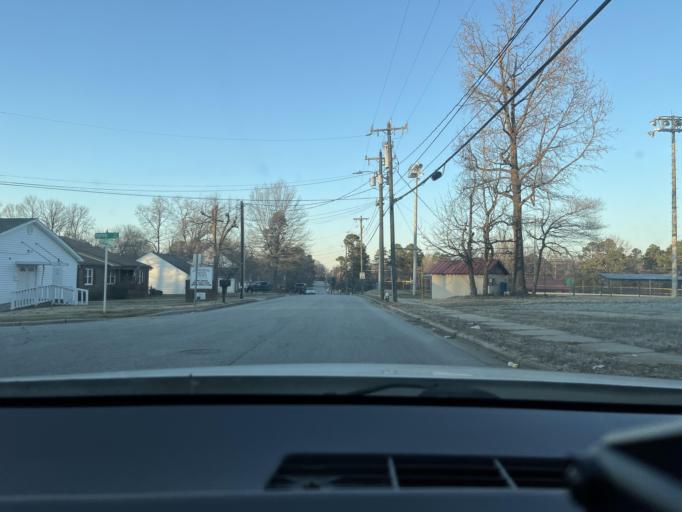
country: US
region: North Carolina
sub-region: Guilford County
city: Greensboro
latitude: 36.0231
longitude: -79.8300
